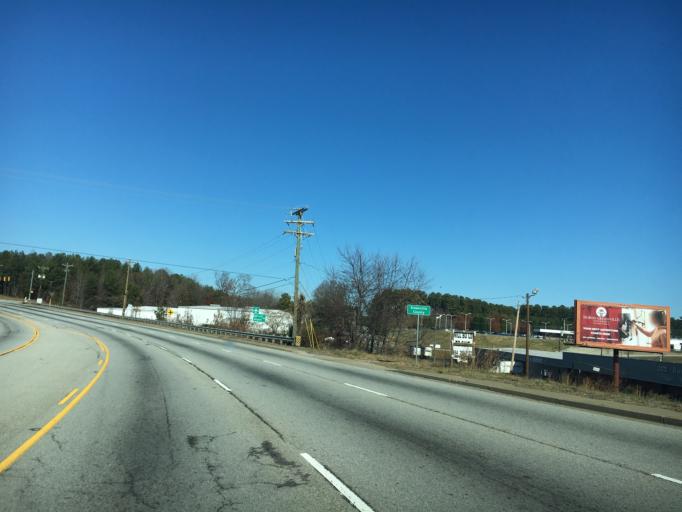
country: US
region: South Carolina
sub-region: Greenville County
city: Greer
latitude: 34.8752
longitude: -82.2251
